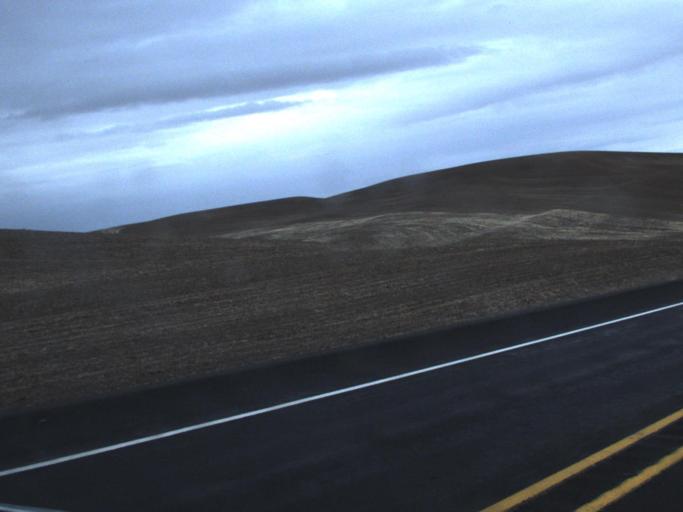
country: US
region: Washington
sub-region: Whitman County
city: Pullman
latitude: 46.6196
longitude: -117.1628
